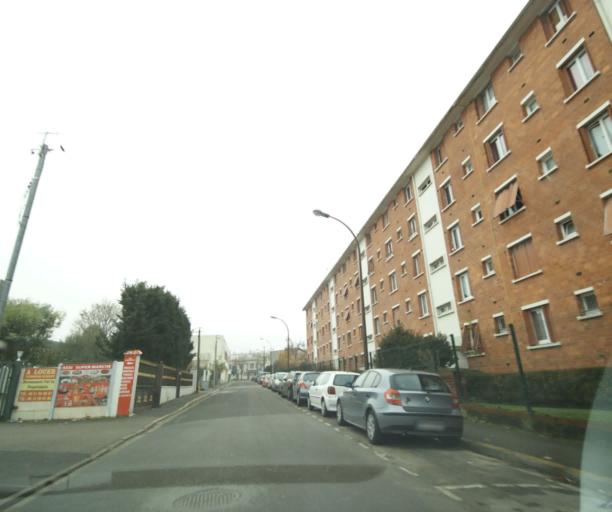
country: FR
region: Ile-de-France
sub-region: Departement de Seine-Saint-Denis
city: Livry-Gargan
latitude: 48.9257
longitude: 2.5465
